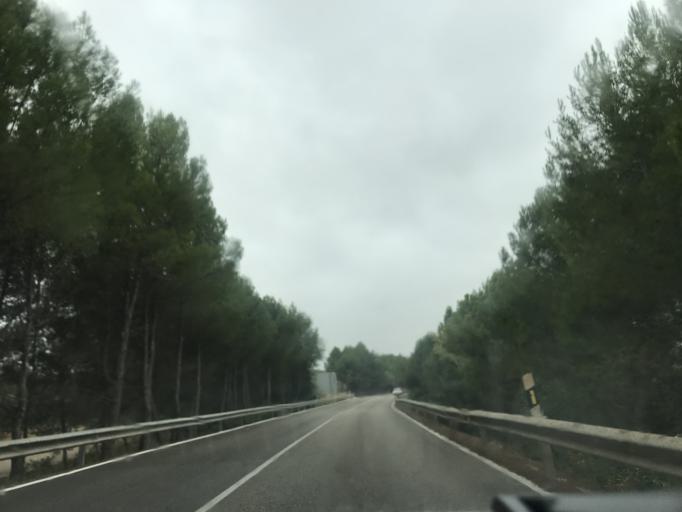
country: ES
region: Andalusia
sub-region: Provincia de Jaen
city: Peal de Becerro
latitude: 37.9144
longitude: -3.0958
